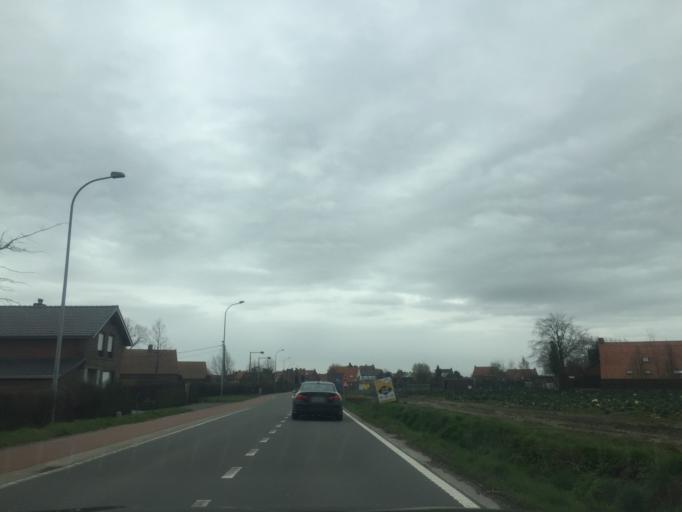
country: BE
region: Flanders
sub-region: Provincie West-Vlaanderen
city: Izegem
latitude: 50.9335
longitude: 3.2092
